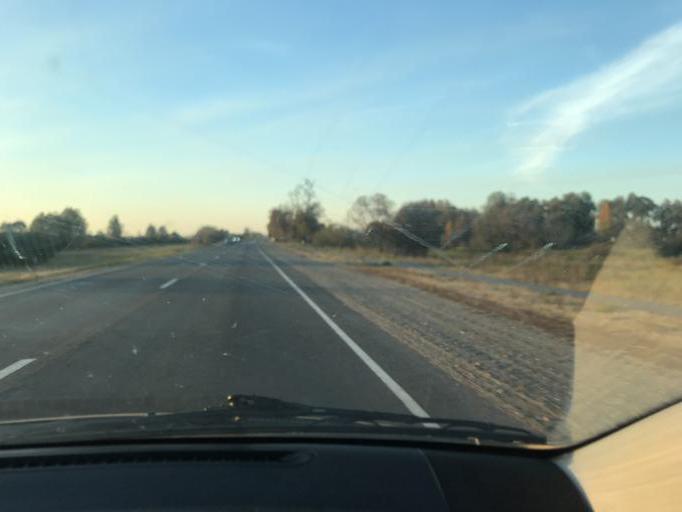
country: BY
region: Brest
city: Pinsk
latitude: 52.0888
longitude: 26.1306
